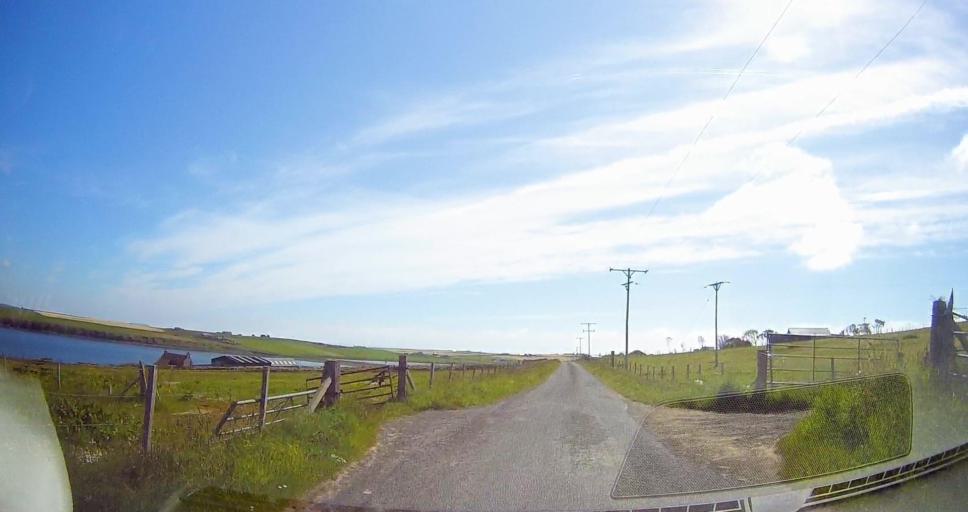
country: GB
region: Scotland
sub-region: Orkney Islands
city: Kirkwall
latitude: 58.8563
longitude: -2.9324
